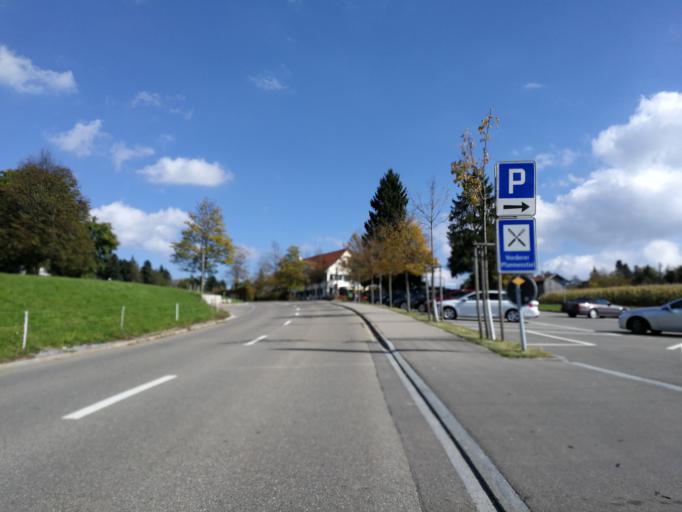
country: CH
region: Zurich
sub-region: Bezirk Uster
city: Egg
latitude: 47.2856
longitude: 8.6797
